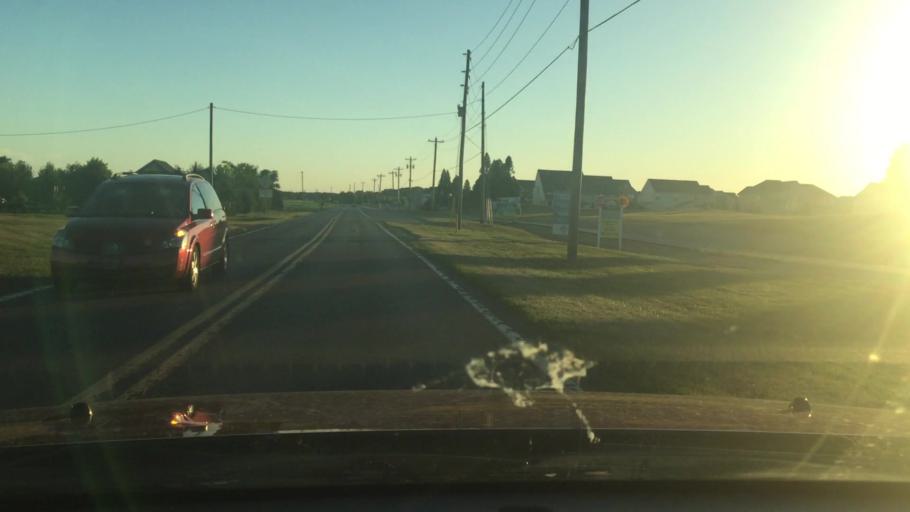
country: US
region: Delaware
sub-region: Kent County
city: Woodside East
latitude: 39.0519
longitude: -75.5195
